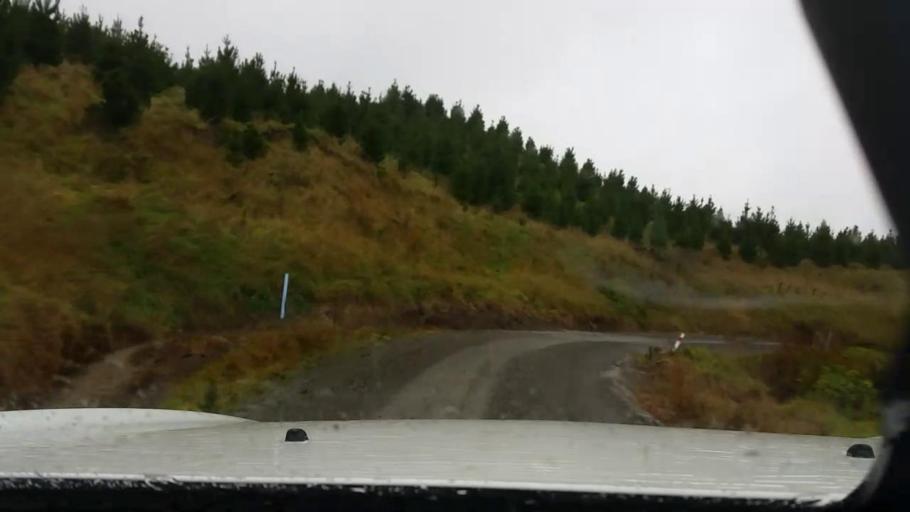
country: NZ
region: Wellington
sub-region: Masterton District
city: Masterton
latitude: -41.1985
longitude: 175.8114
